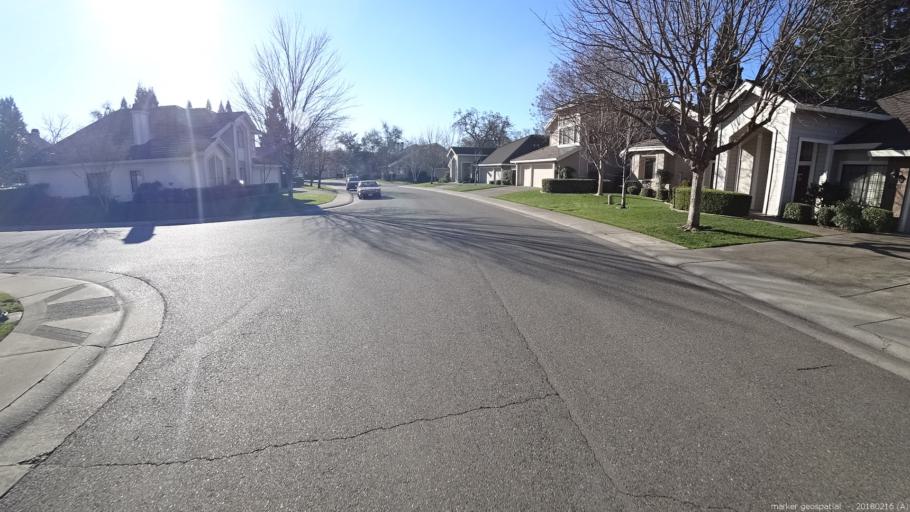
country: US
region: California
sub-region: Sacramento County
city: Gold River
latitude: 38.6256
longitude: -121.2430
